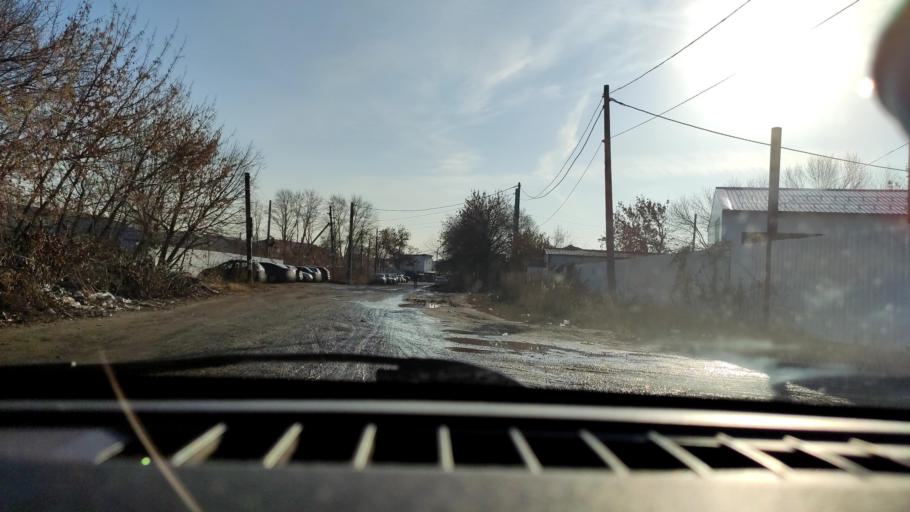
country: RU
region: Samara
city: Samara
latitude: 53.1175
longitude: 50.1147
